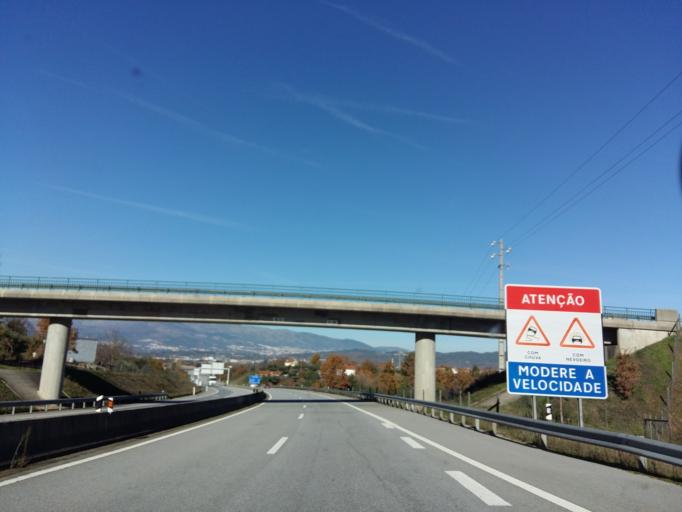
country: PT
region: Castelo Branco
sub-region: Concelho do Fundao
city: Fundao
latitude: 40.1409
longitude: -7.4784
